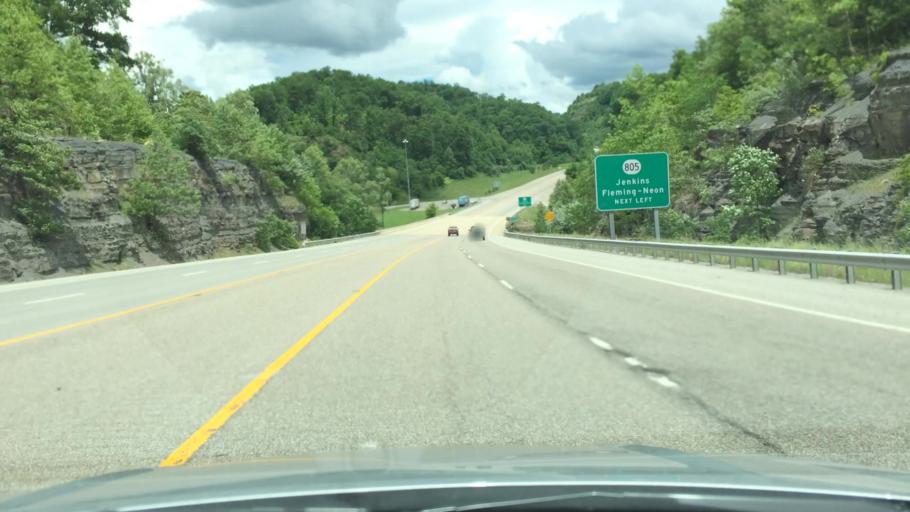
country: US
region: Kentucky
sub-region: Letcher County
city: Jenkins
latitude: 37.1743
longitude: -82.6427
